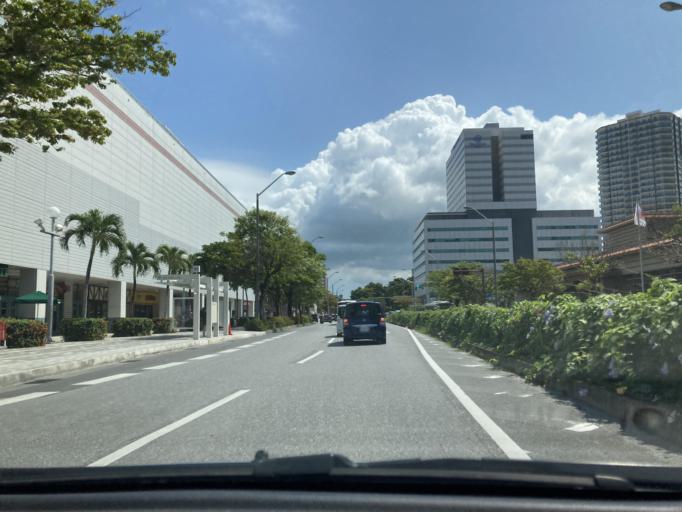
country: JP
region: Okinawa
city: Naha-shi
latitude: 26.2251
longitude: 127.6943
